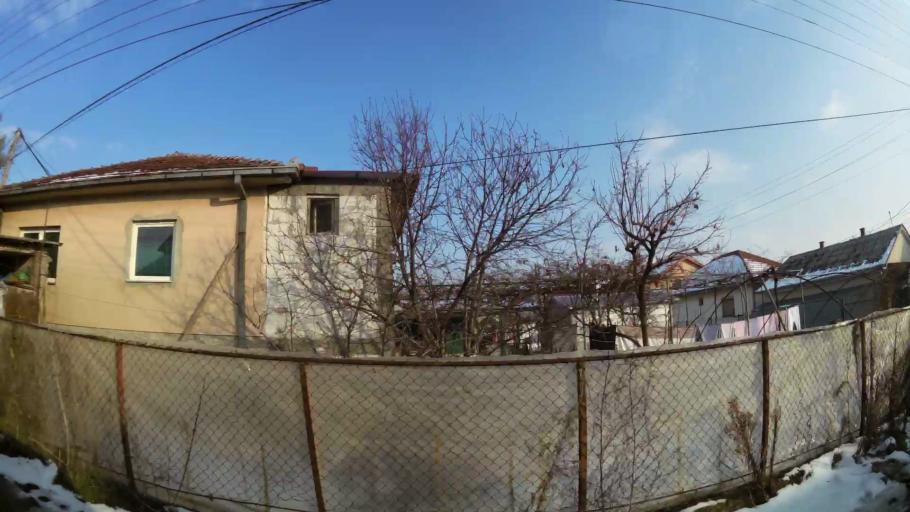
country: MK
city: Creshevo
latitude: 42.0331
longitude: 21.5180
